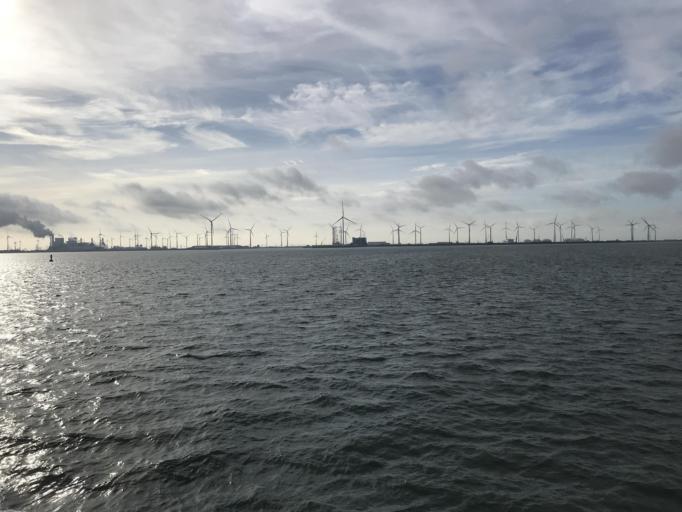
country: NL
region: Groningen
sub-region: Gemeente Appingedam
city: Appingedam
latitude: 53.4845
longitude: 6.8389
